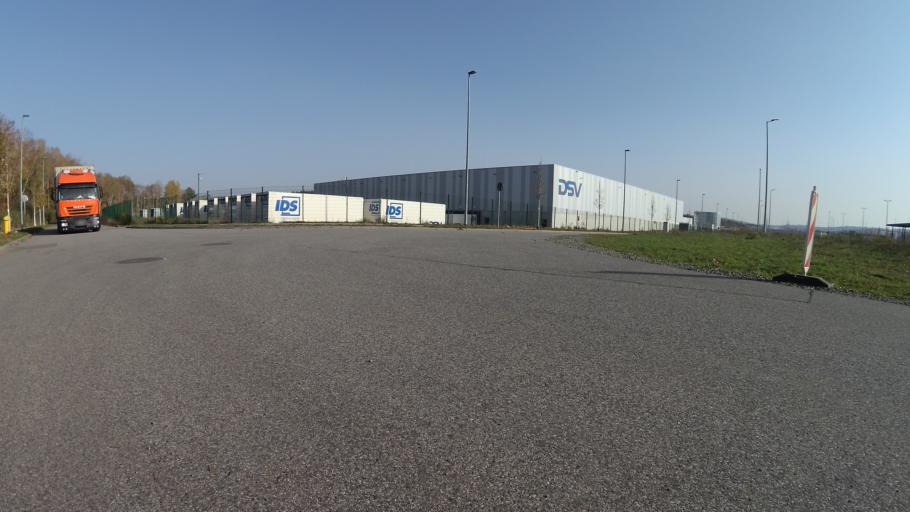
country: DE
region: Saarland
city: Homburg
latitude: 49.3339
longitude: 7.3004
